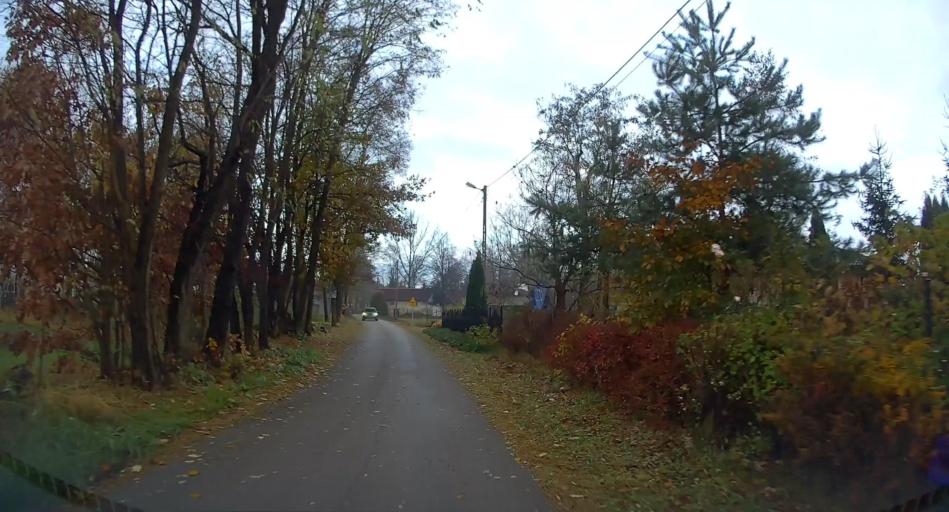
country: PL
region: Lodz Voivodeship
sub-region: Powiat skierniewicki
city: Kowiesy
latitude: 51.9379
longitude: 20.4004
